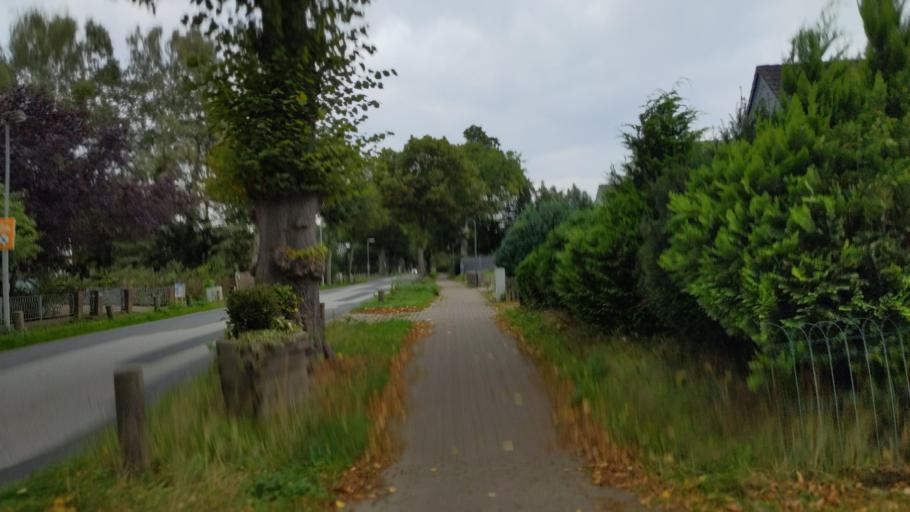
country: DE
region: Schleswig-Holstein
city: Krummesse
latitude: 53.7880
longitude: 10.6404
